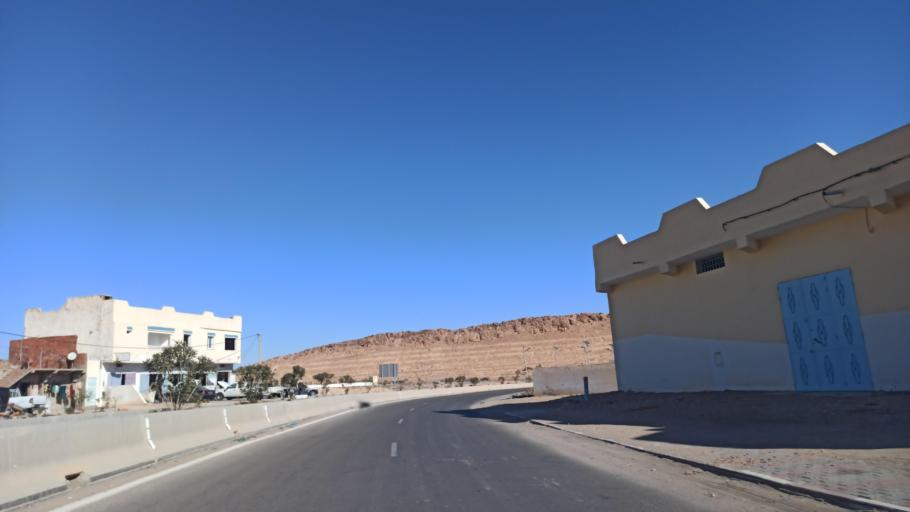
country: TN
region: Gafsa
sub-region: Gafsa Municipality
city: Gafsa
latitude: 34.4503
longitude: 8.7732
